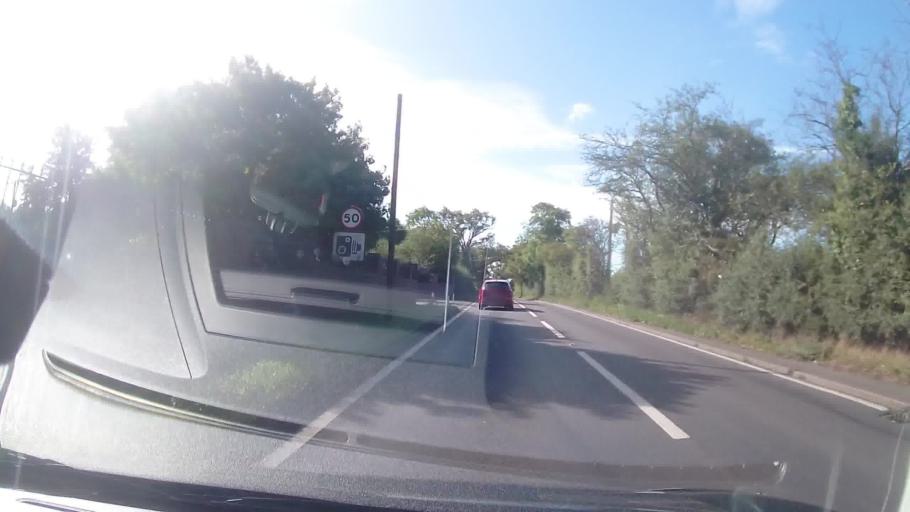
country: GB
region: England
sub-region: Shropshire
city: Astley
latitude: 52.7646
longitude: -2.7147
